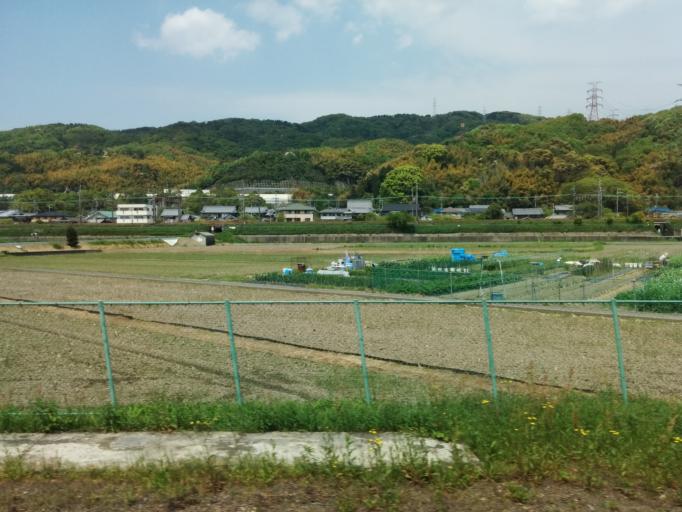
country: JP
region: Osaka
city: Takatsuki
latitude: 34.8643
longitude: 135.6531
